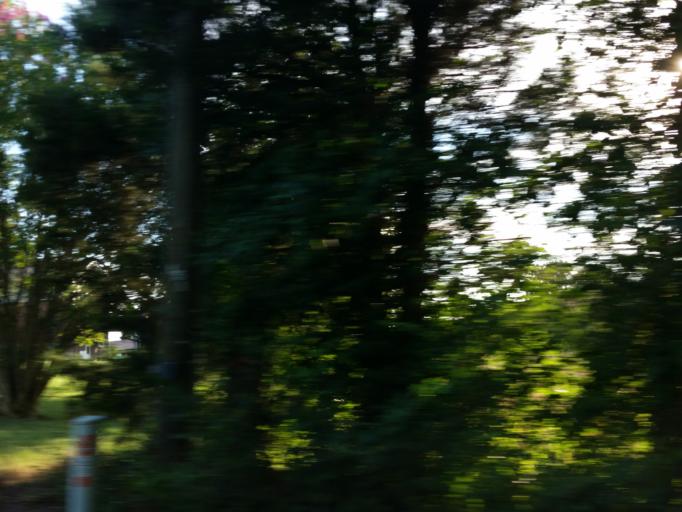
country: US
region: Tennessee
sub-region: Blount County
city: Eagleton Village
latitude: 35.8621
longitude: -83.9134
